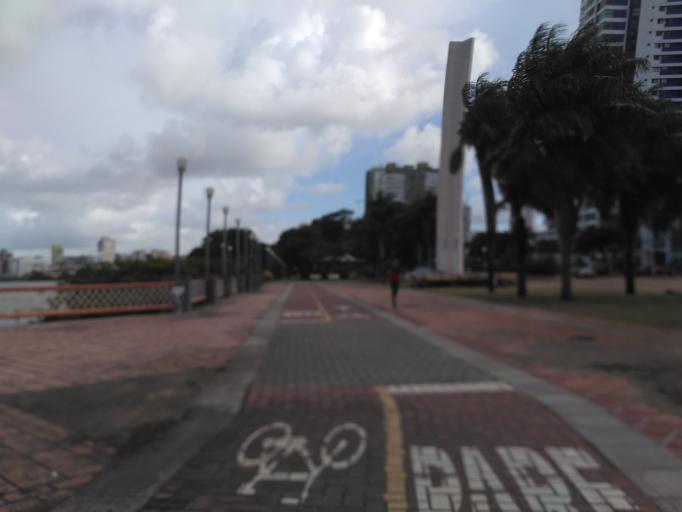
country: BR
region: Pernambuco
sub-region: Recife
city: Recife
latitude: -8.0525
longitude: -34.8750
